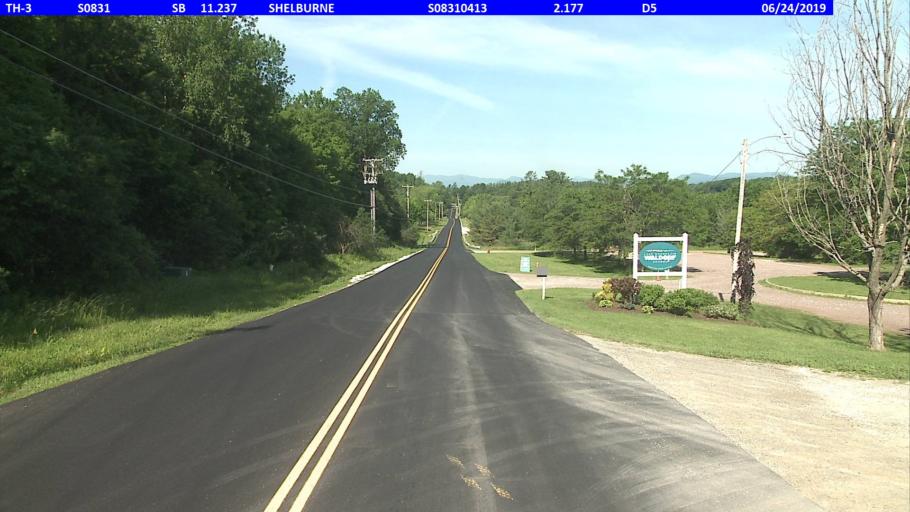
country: US
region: Vermont
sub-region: Chittenden County
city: Burlington
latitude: 44.3692
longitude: -73.2338
